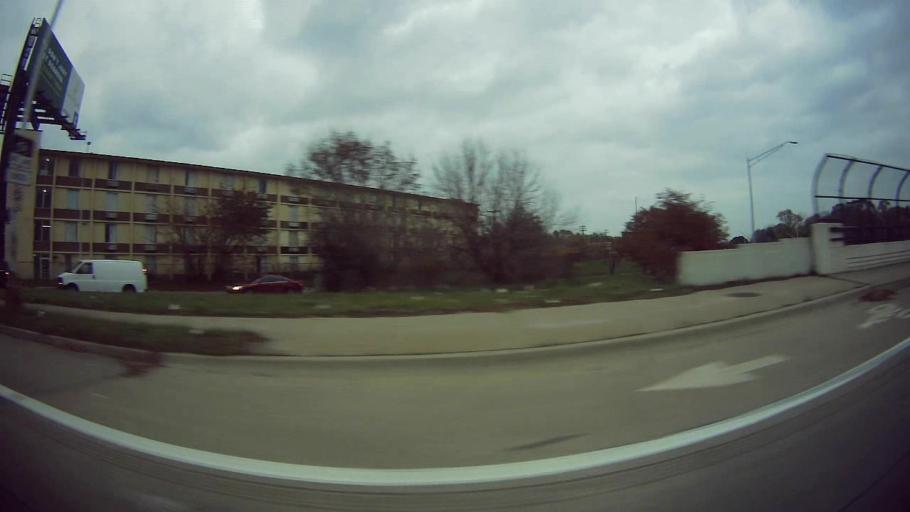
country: US
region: Michigan
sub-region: Wayne County
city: Grosse Pointe Park
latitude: 42.3968
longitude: -82.9881
